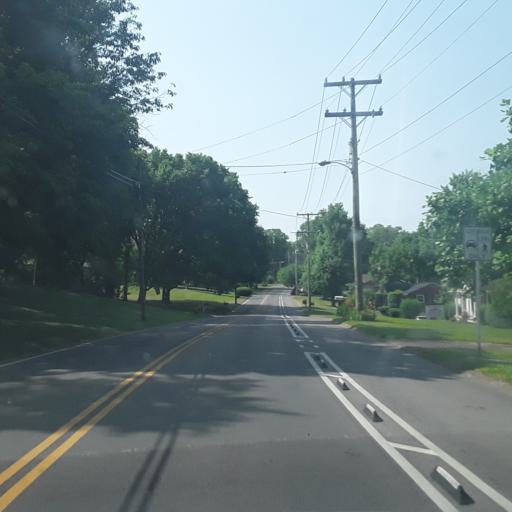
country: US
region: Tennessee
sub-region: Williamson County
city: Brentwood
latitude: 36.0503
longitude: -86.7506
